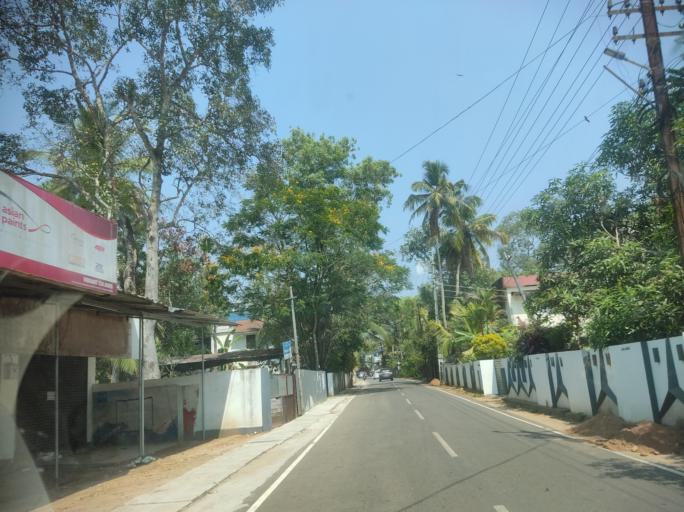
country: IN
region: Kerala
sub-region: Alappuzha
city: Vayalar
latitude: 9.6869
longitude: 76.3324
